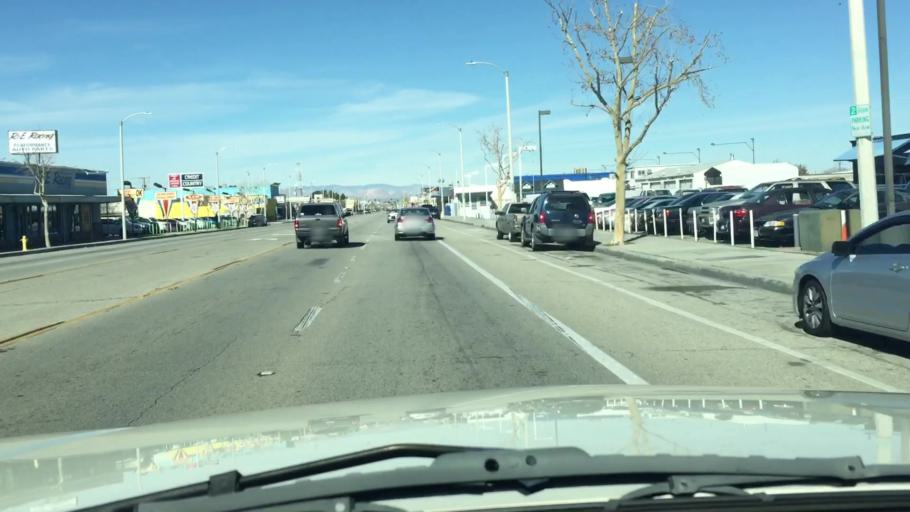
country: US
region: California
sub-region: Los Angeles County
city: Lancaster
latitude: 34.6915
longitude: -118.1358
